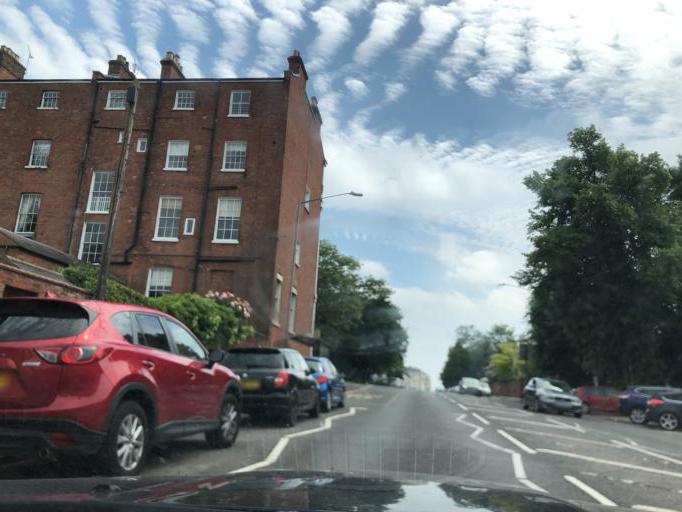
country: GB
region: England
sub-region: Warwickshire
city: Royal Leamington Spa
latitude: 52.2953
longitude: -1.5401
